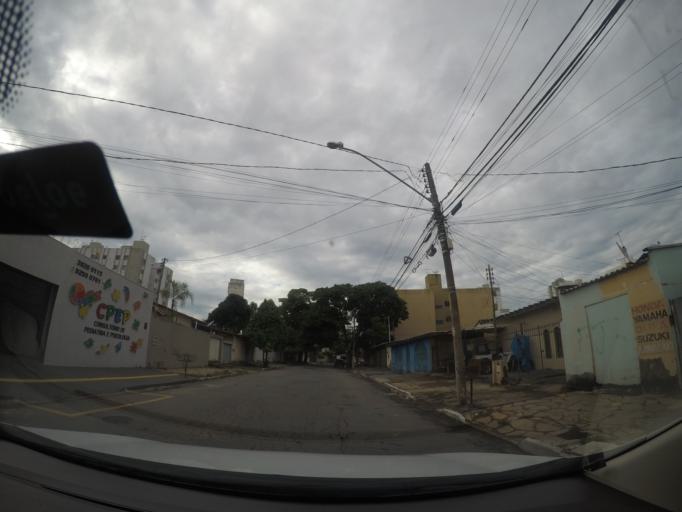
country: BR
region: Goias
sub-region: Goiania
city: Goiania
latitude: -16.6668
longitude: -49.2662
